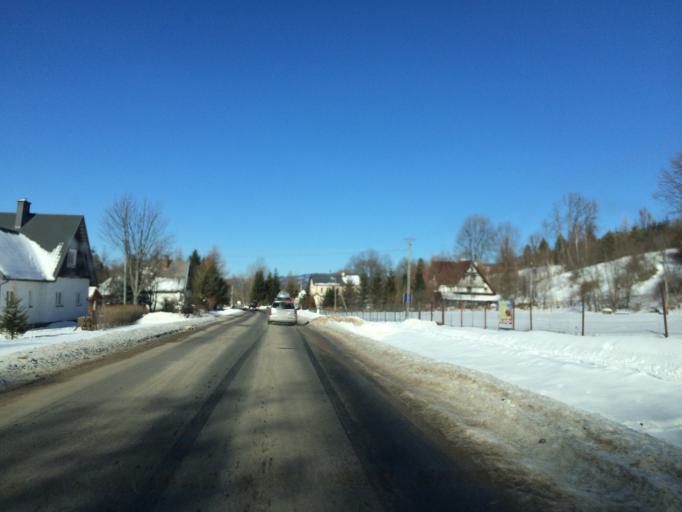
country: PL
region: Subcarpathian Voivodeship
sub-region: Powiat leski
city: Cisna
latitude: 49.1543
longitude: 22.4702
